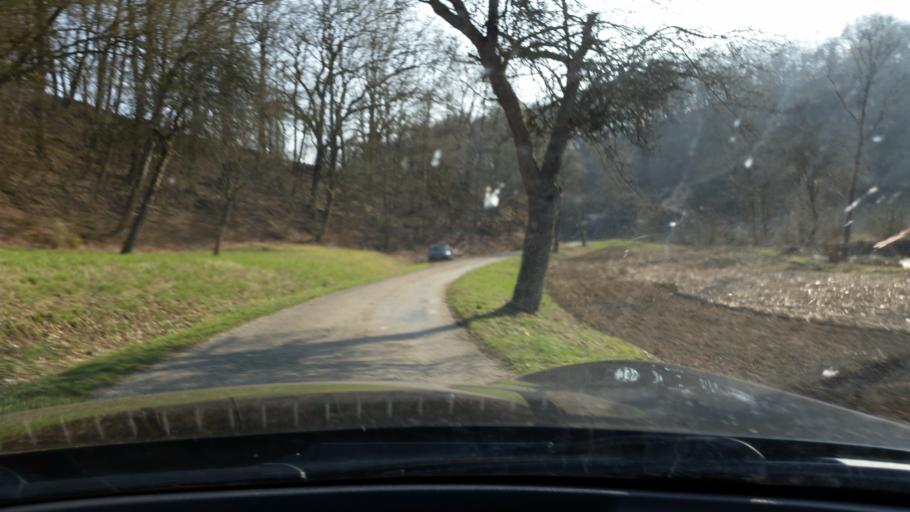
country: DE
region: Baden-Wuerttemberg
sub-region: Regierungsbezirk Stuttgart
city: Mockmuhl
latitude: 49.3221
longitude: 9.3899
